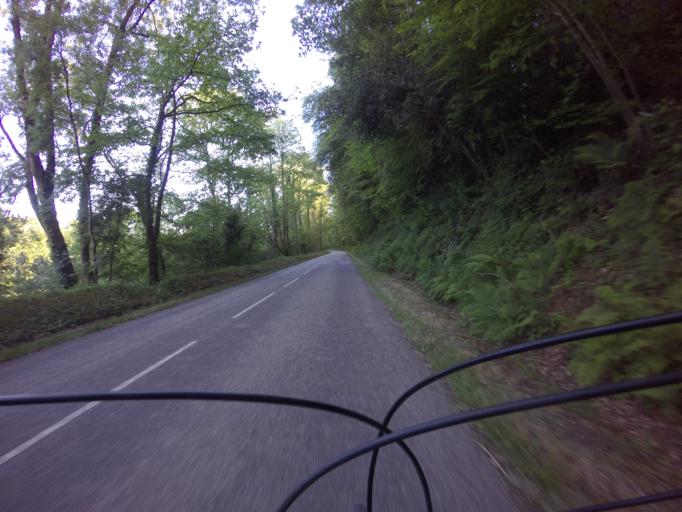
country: FR
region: Brittany
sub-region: Departement du Finistere
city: Quimper
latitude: 48.0244
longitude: -4.1432
